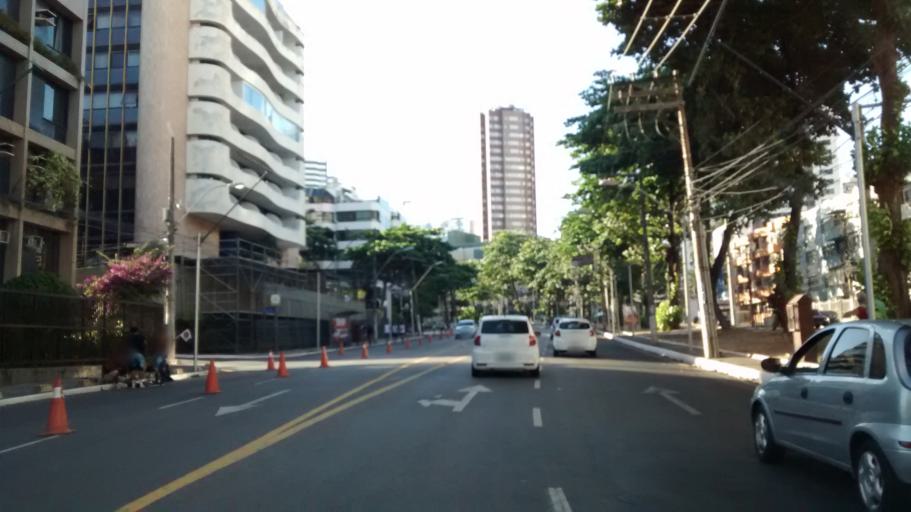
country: BR
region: Bahia
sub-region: Salvador
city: Salvador
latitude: -13.0092
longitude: -38.5148
